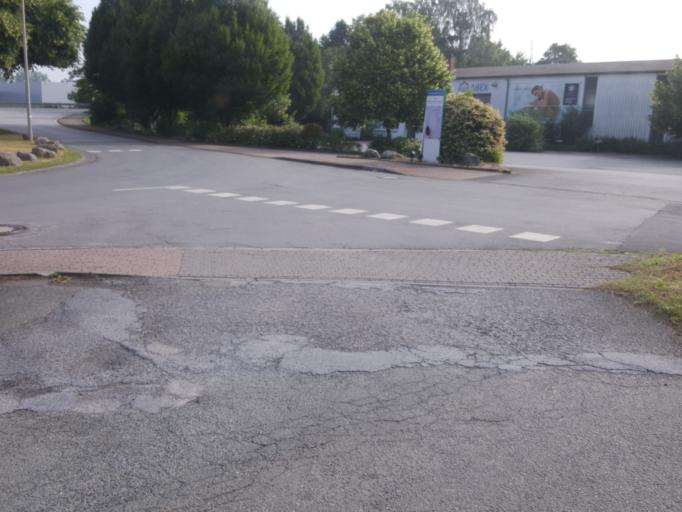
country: DE
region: North Rhine-Westphalia
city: Loehne
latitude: 52.1993
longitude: 8.7416
